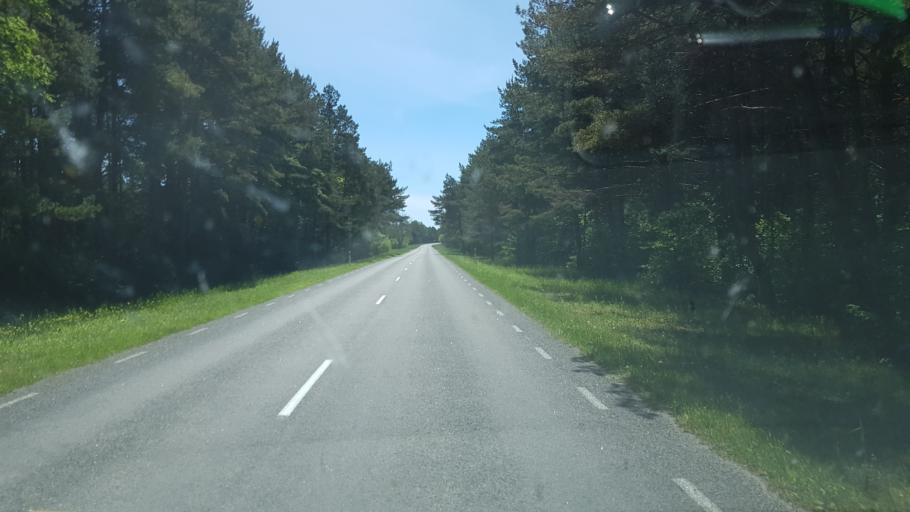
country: EE
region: Saare
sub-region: Kuressaare linn
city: Kuressaare
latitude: 58.1292
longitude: 22.2463
